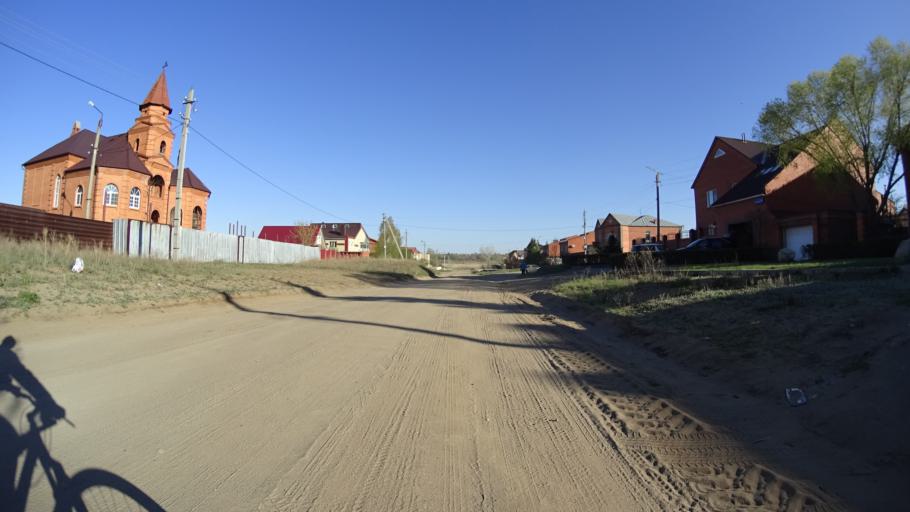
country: RU
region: Chelyabinsk
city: Troitsk
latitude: 54.0715
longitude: 61.5361
